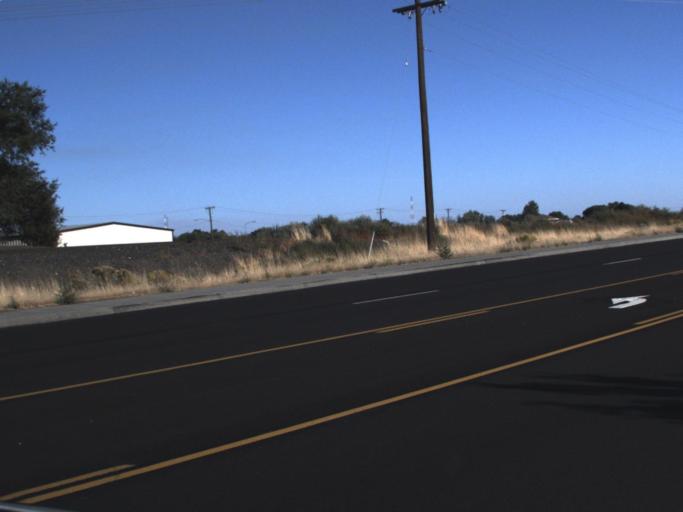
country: US
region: Washington
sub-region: Franklin County
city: Pasco
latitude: 46.2025
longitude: -119.0974
